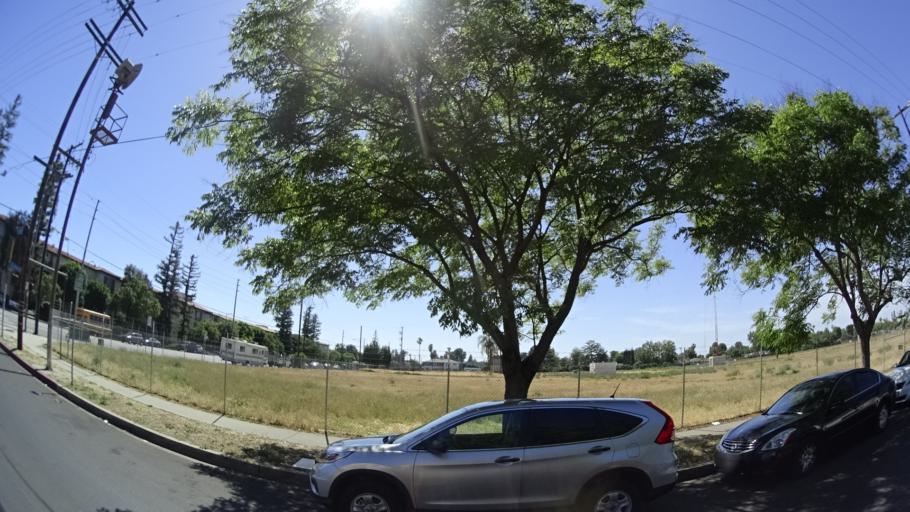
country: US
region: California
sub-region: Los Angeles County
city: North Hollywood
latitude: 34.1724
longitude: -118.4094
